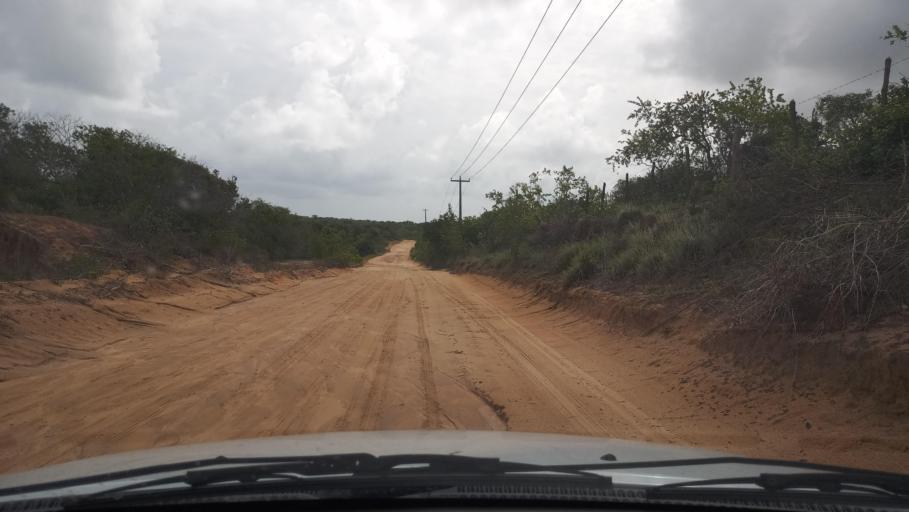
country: BR
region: Rio Grande do Norte
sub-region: Maxaranguape
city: Sao Miguel
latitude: -5.4837
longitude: -35.3069
